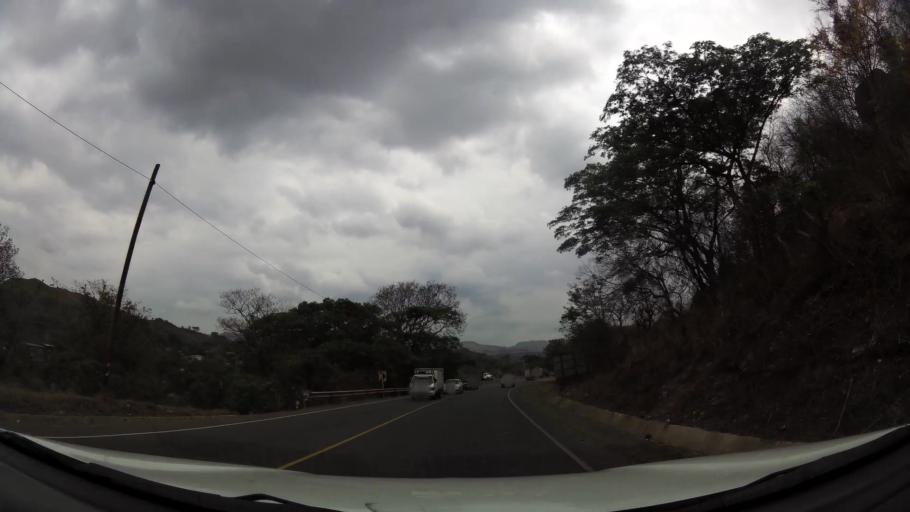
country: NI
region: Matagalpa
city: Matagalpa
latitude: 12.9172
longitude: -85.9364
